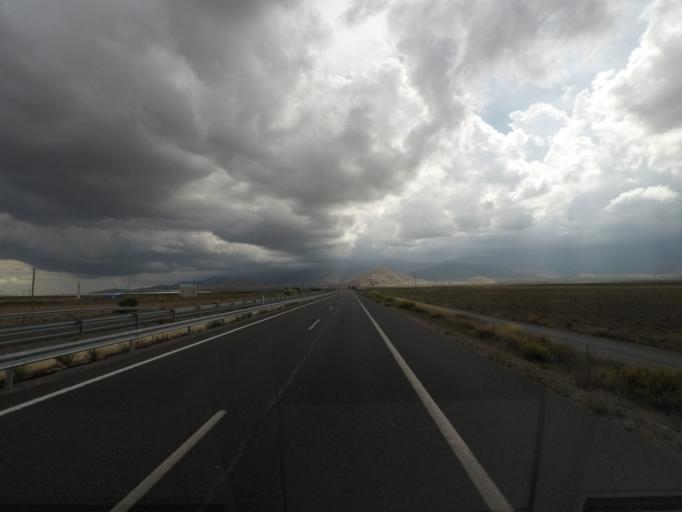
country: ES
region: Andalusia
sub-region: Provincia de Granada
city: Alquife
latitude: 37.2192
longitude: -3.0756
